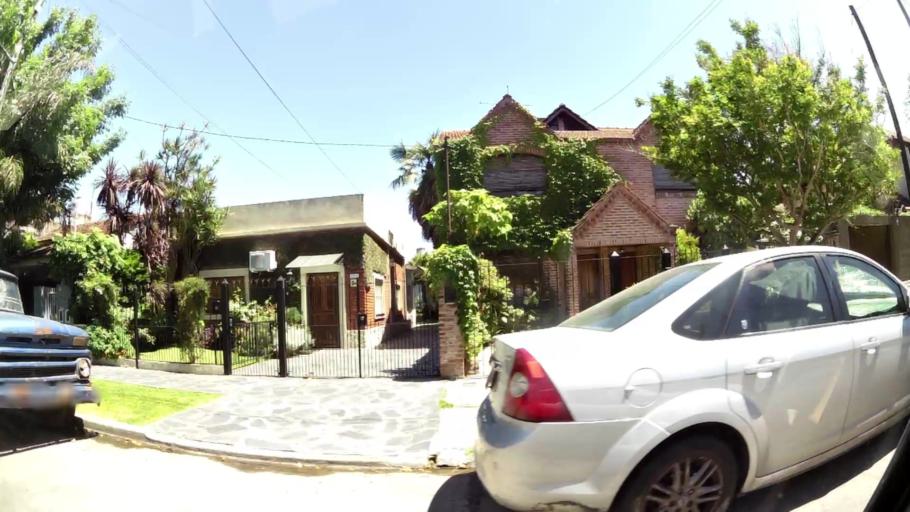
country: AR
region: Buenos Aires
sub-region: Partido de San Isidro
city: San Isidro
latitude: -34.4927
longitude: -58.5122
